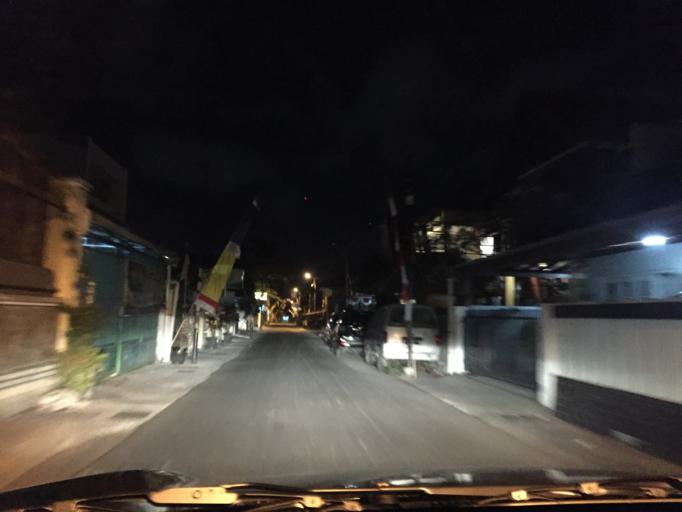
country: ID
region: Daerah Istimewa Yogyakarta
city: Yogyakarta
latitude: -7.7940
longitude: 110.3709
